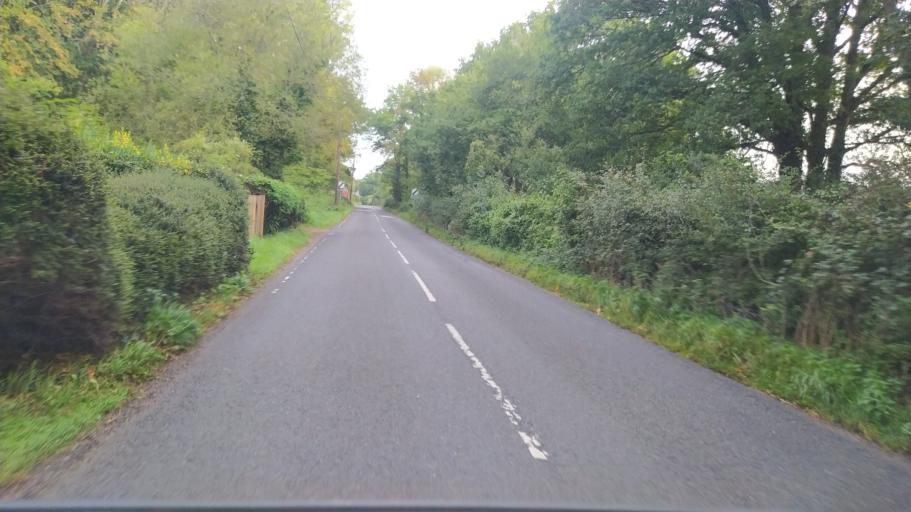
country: GB
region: England
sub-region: Hampshire
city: East Dean
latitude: 51.0465
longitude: -1.5504
